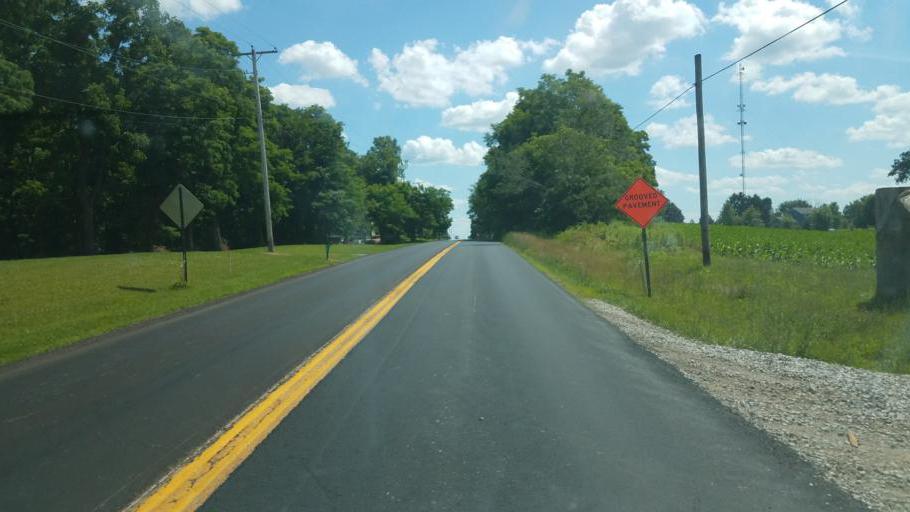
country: US
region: Ohio
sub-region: Knox County
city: Fredericktown
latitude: 40.5054
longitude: -82.6737
